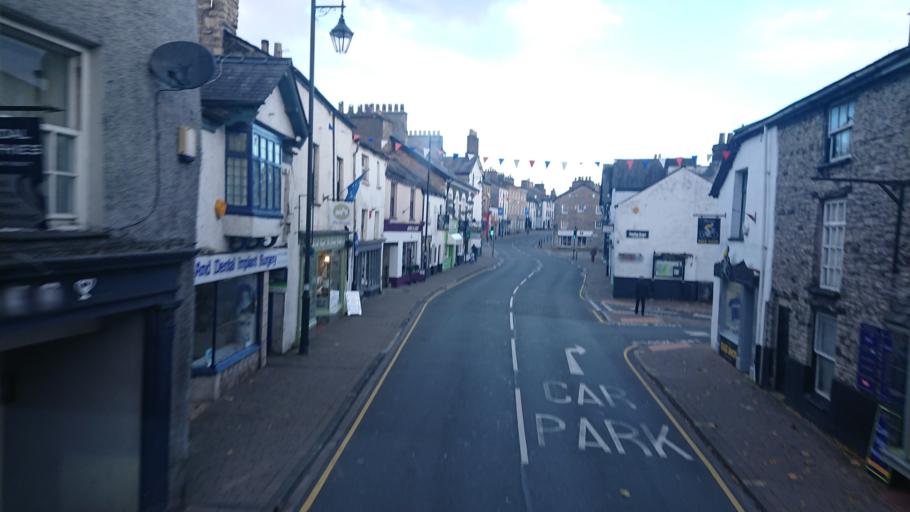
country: GB
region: England
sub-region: Cumbria
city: Kendal
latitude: 54.3228
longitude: -2.7464
